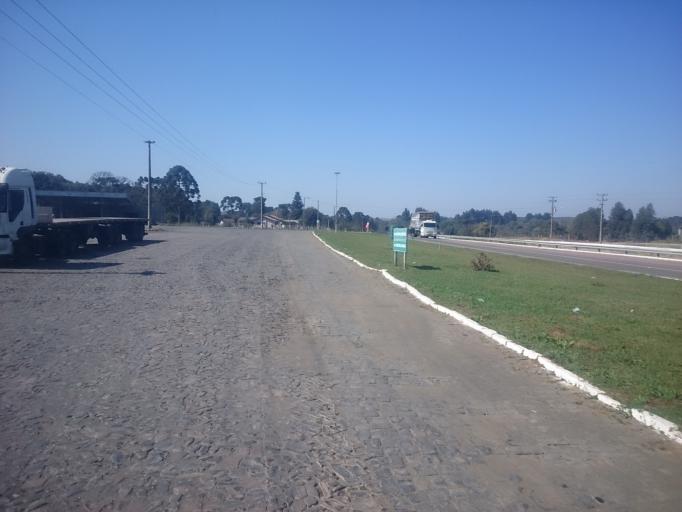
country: BR
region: Santa Catarina
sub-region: Canoinhas
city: Canoinhas
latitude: -26.3775
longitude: -50.1975
